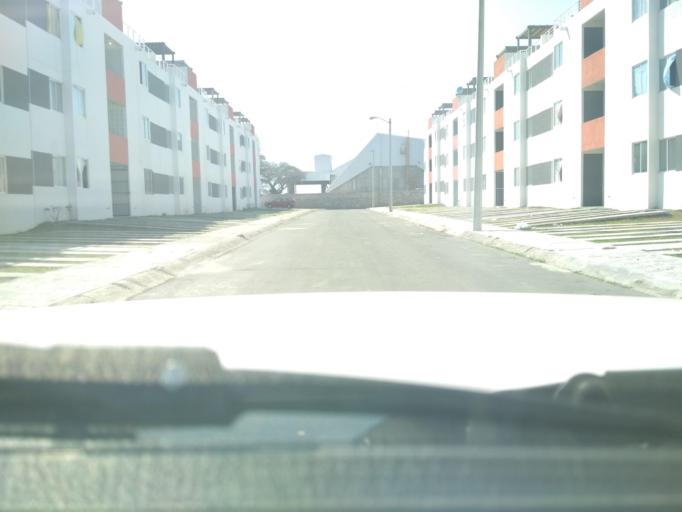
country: MX
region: Veracruz
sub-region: Veracruz
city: Las Amapolas
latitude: 19.1563
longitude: -96.2236
